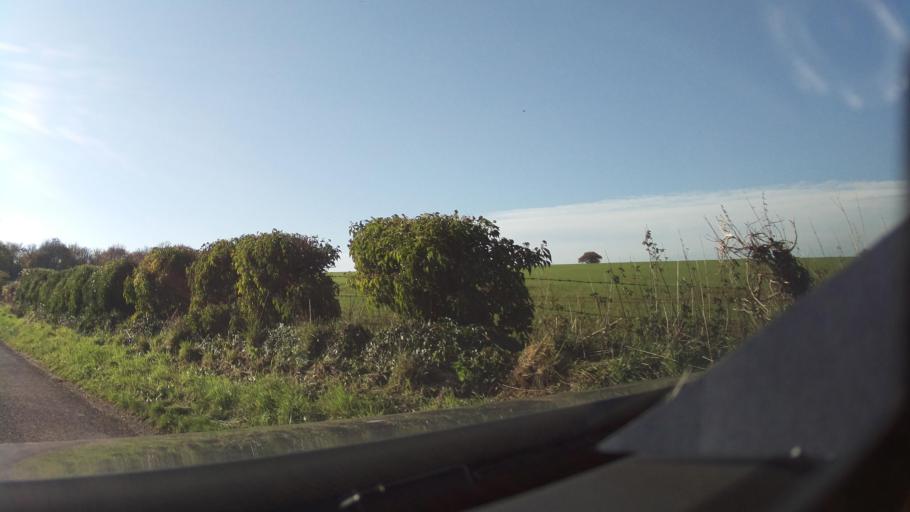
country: GB
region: England
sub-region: Somerset
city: Castle Cary
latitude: 51.0404
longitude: -2.4871
